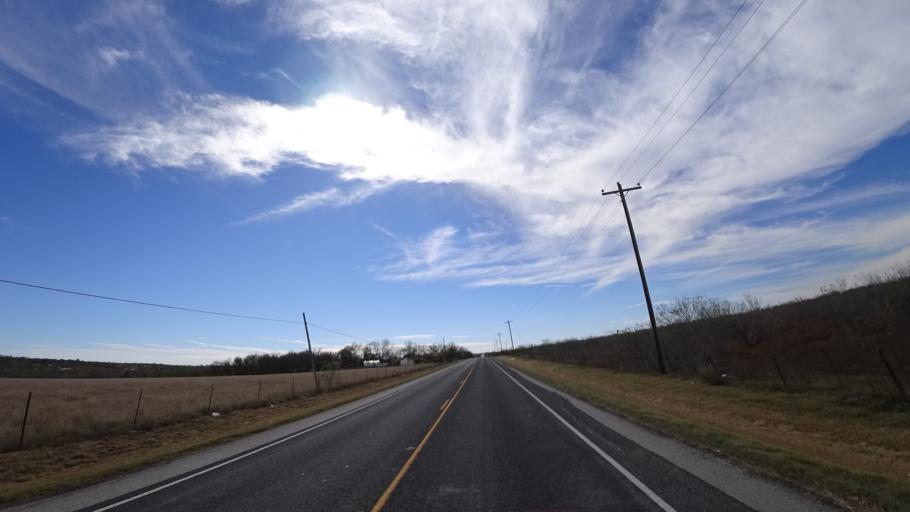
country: US
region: Texas
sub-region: Travis County
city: Onion Creek
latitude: 30.1235
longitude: -97.7136
